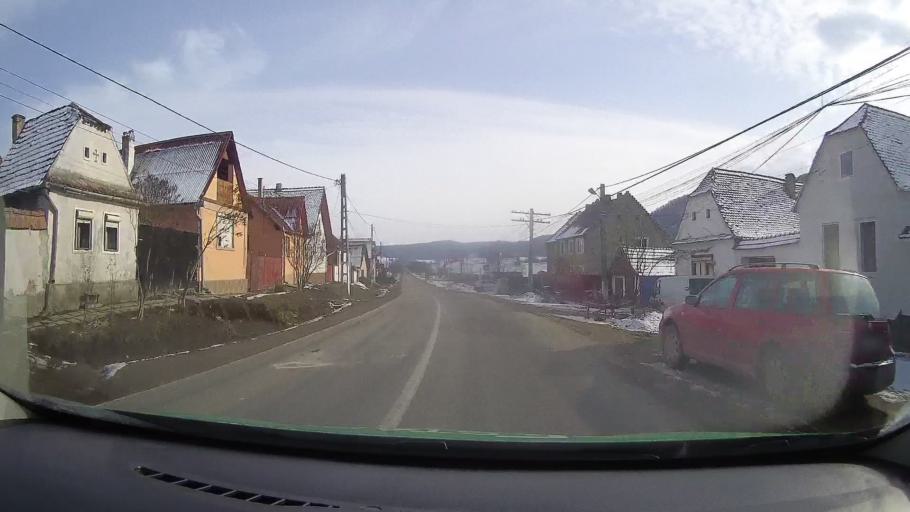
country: RO
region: Mures
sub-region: Comuna Apold
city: Saes
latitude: 46.1501
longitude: 24.7715
